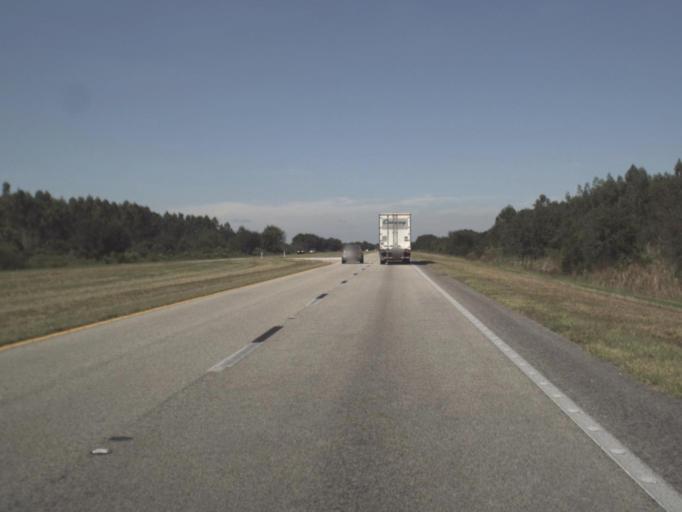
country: US
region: Florida
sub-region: Highlands County
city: Placid Lakes
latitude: 27.0118
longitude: -81.3345
